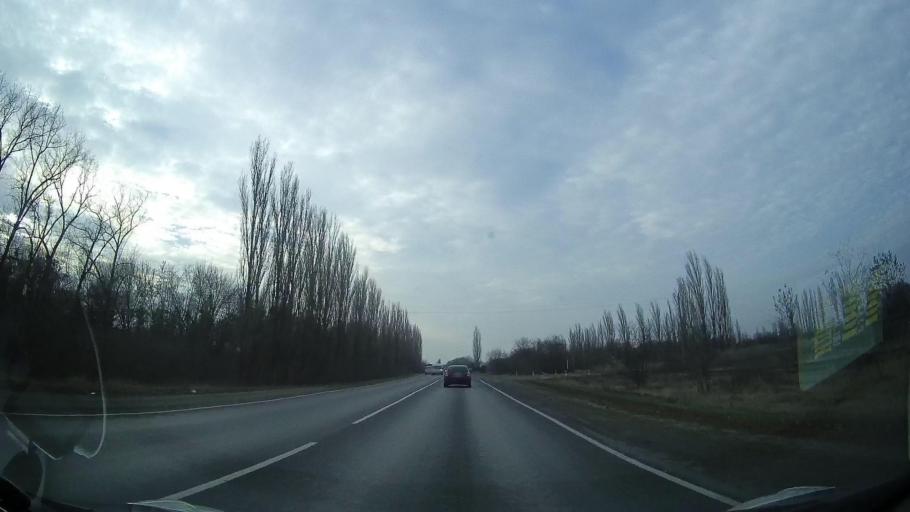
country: RU
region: Rostov
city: Ol'ginskaya
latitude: 47.1394
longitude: 40.0114
